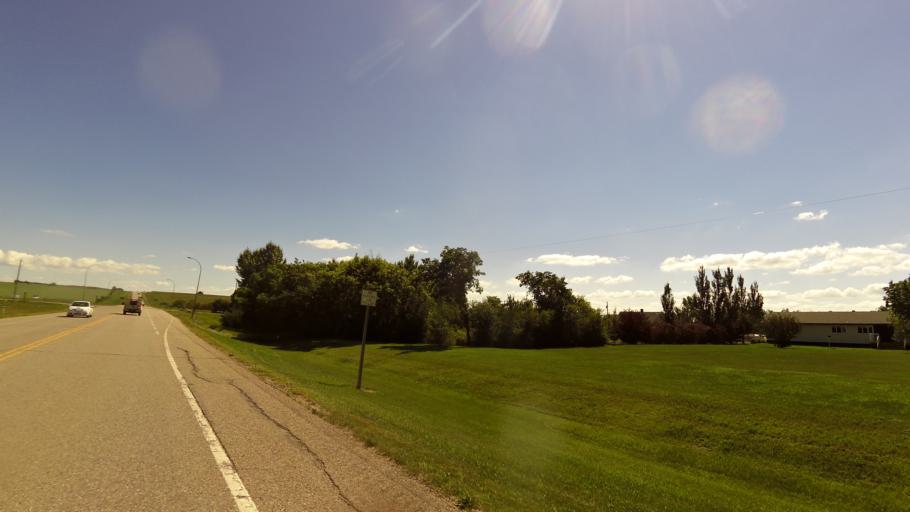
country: CA
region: Saskatchewan
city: Lloydminster
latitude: 52.8417
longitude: -110.0203
